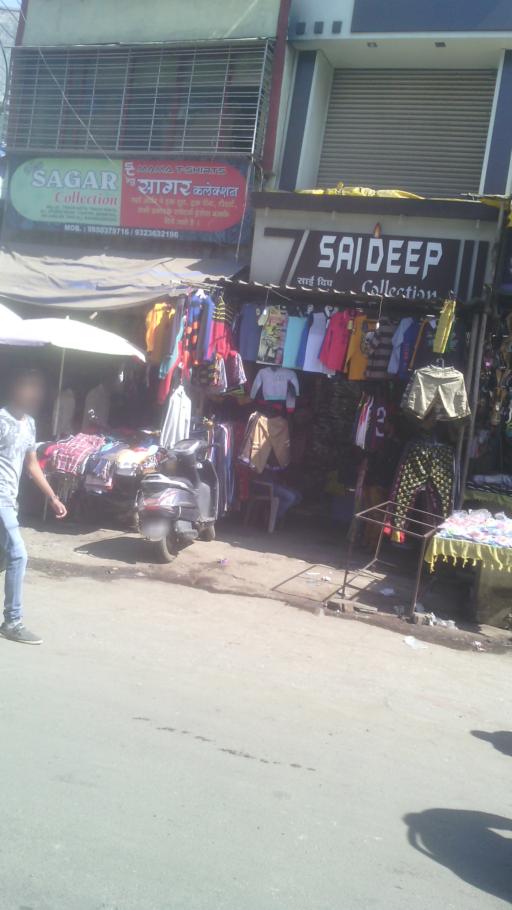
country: IN
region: Maharashtra
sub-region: Thane
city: Ulhasnagar
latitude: 19.2313
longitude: 73.1608
